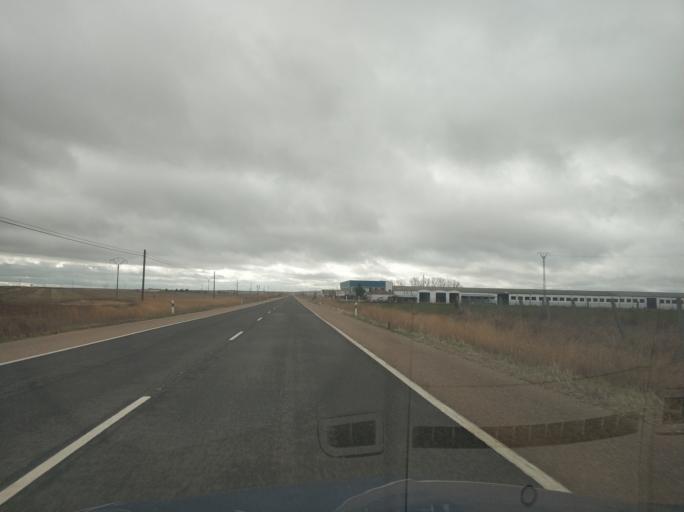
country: ES
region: Castille and Leon
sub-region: Provincia de Salamanca
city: Castellanos de Moriscos
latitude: 41.0400
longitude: -5.5701
